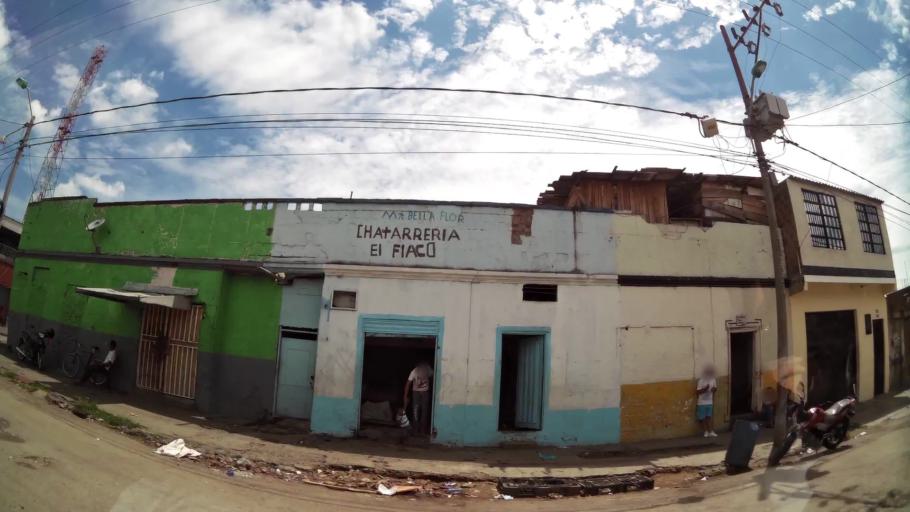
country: CO
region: Valle del Cauca
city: Cali
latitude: 3.4458
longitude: -76.5232
